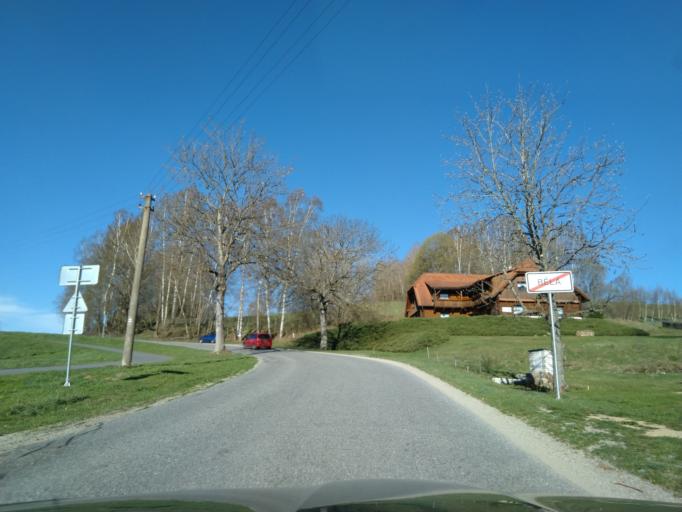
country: CZ
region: Jihocesky
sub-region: Okres Cesky Krumlov
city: Horni Plana
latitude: 48.7954
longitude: 13.9618
